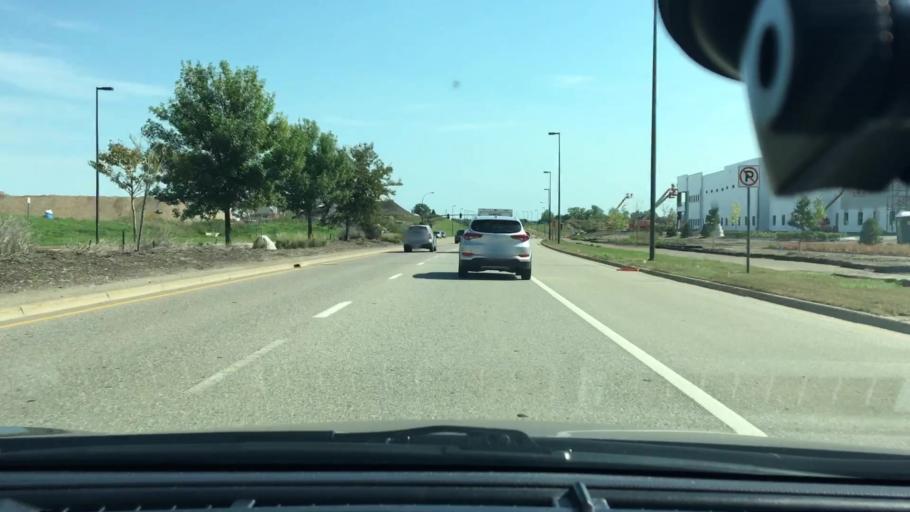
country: US
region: Minnesota
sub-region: Hennepin County
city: Osseo
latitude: 45.0944
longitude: -93.4154
